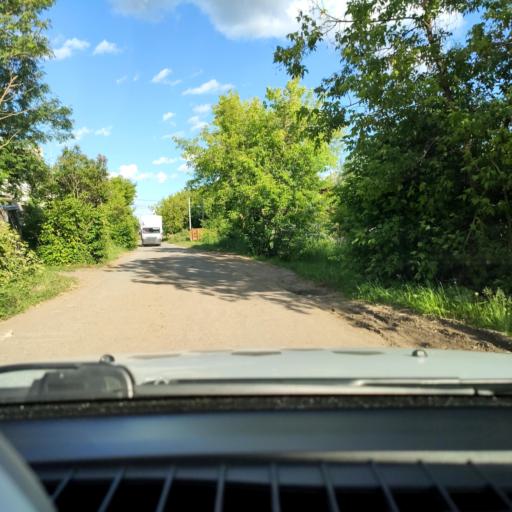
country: RU
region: Perm
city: Ferma
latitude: 57.9054
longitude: 56.2994
